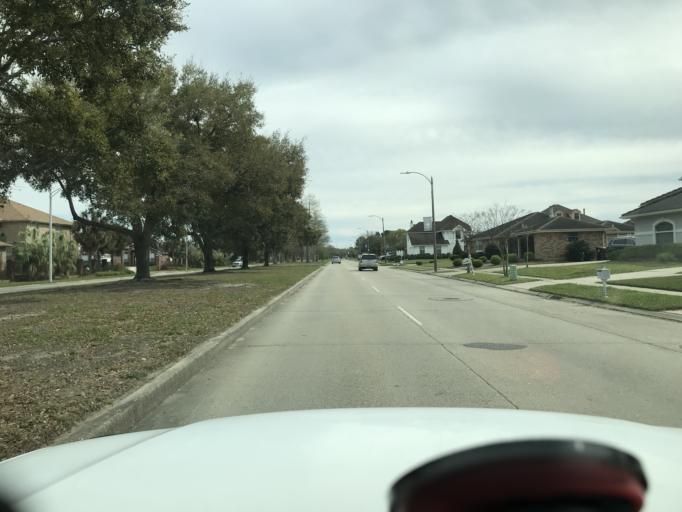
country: US
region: Louisiana
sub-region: Saint Bernard Parish
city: Chalmette
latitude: 30.0351
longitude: -89.9521
